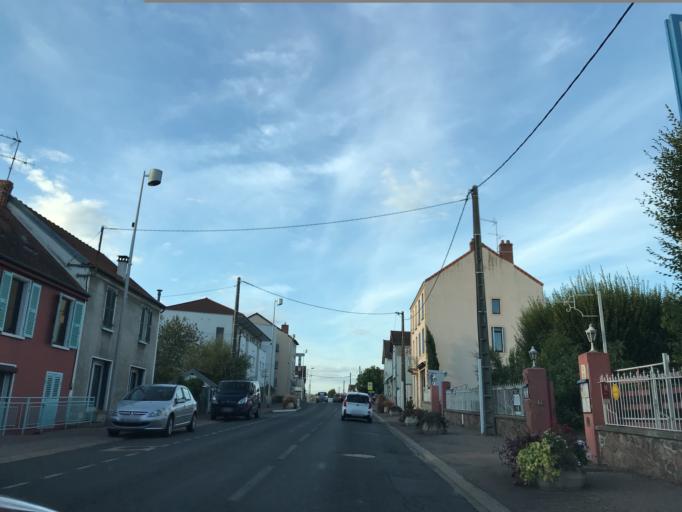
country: FR
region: Auvergne
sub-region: Departement de l'Allier
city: Saint-Yorre
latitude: 46.0658
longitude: 3.4652
